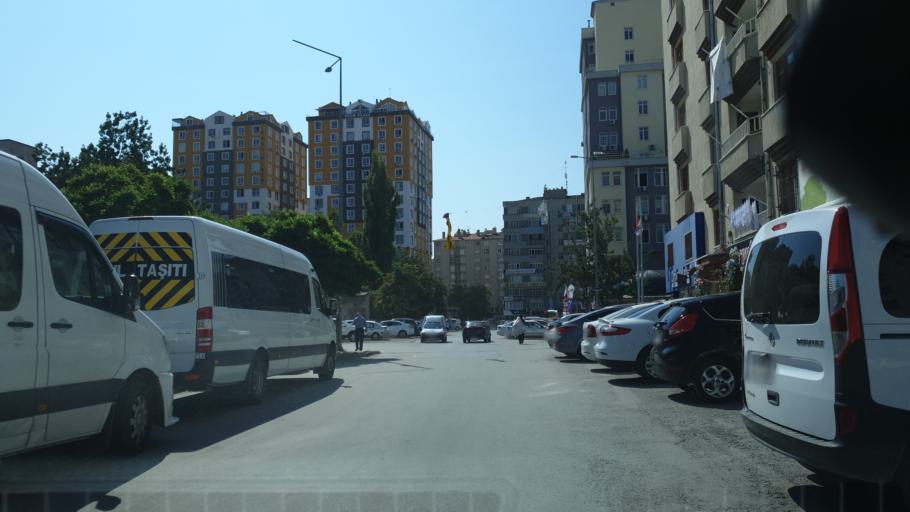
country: TR
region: Kayseri
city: Kayseri
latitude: 38.7259
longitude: 35.4917
